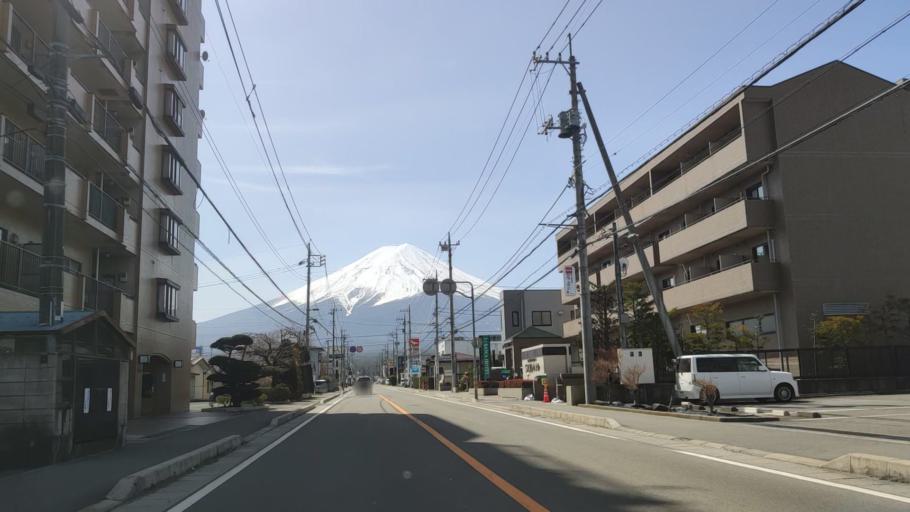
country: JP
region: Yamanashi
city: Fujikawaguchiko
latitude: 35.4949
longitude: 138.7641
